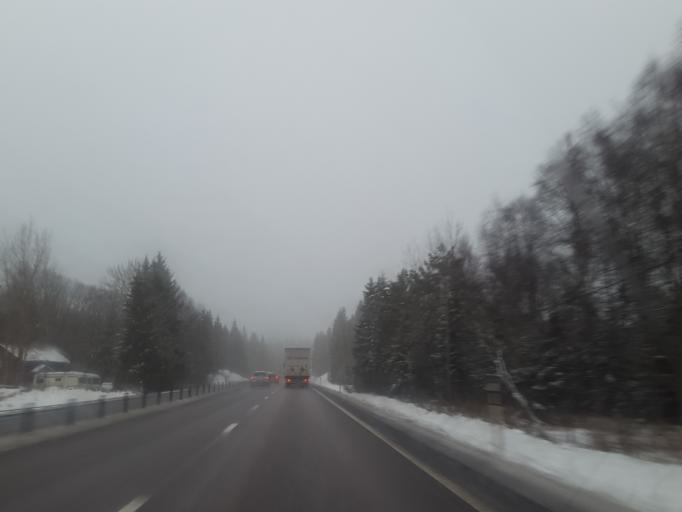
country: SE
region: Joenkoeping
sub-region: Mullsjo Kommun
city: Mullsjoe
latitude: 57.7734
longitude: 13.7002
